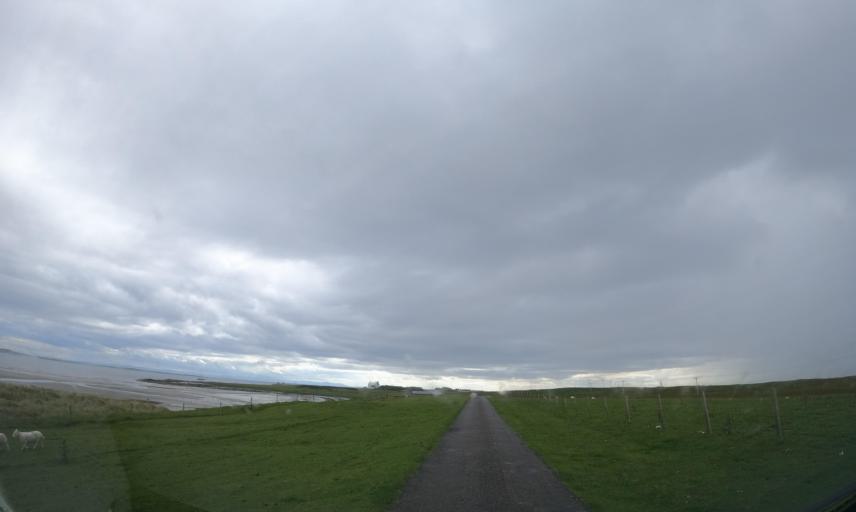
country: GB
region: Scotland
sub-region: Eilean Siar
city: Barra
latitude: 56.5125
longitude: -6.8154
